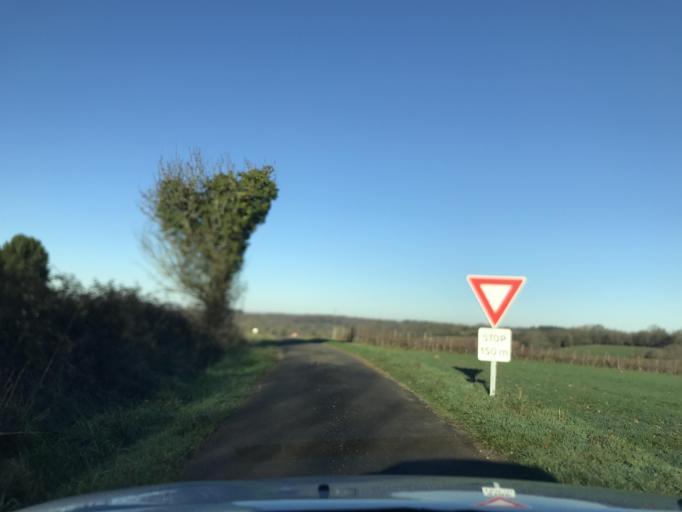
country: FR
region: Poitou-Charentes
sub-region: Departement de la Charente
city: Chasseneuil-sur-Bonnieure
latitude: 45.8429
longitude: 0.4958
